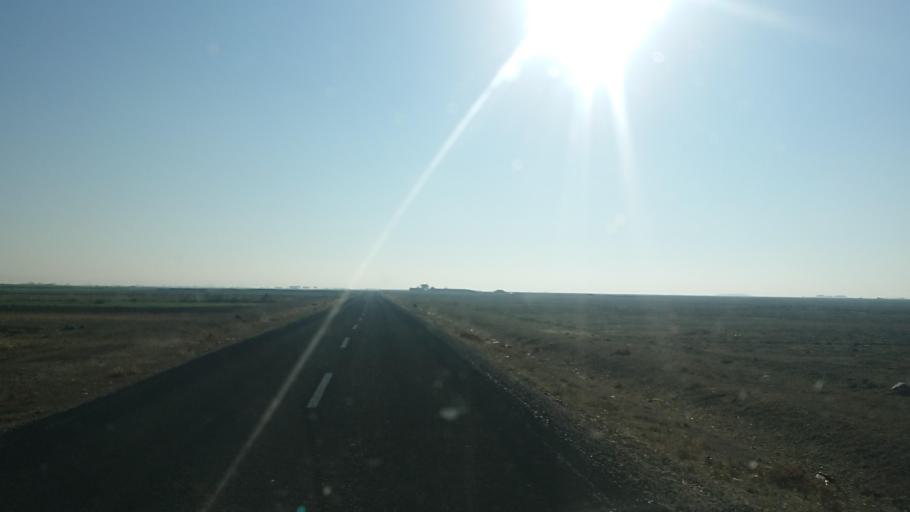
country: TR
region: Aksaray
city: Yesilova
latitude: 38.3876
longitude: 33.7966
